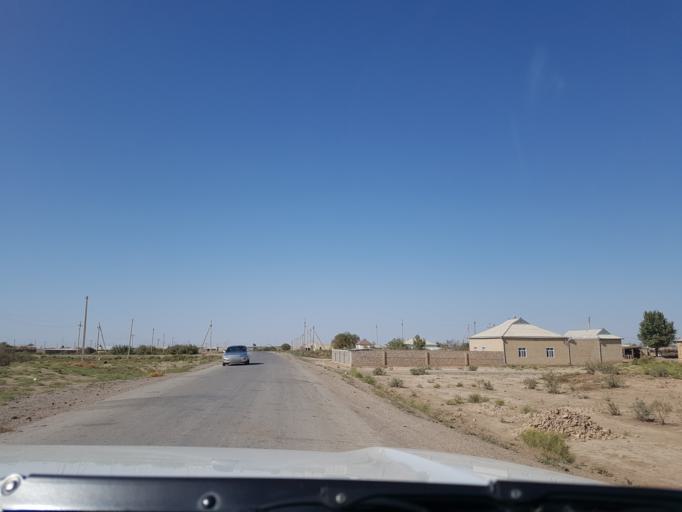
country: IR
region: Razavi Khorasan
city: Sarakhs
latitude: 36.5145
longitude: 61.2529
